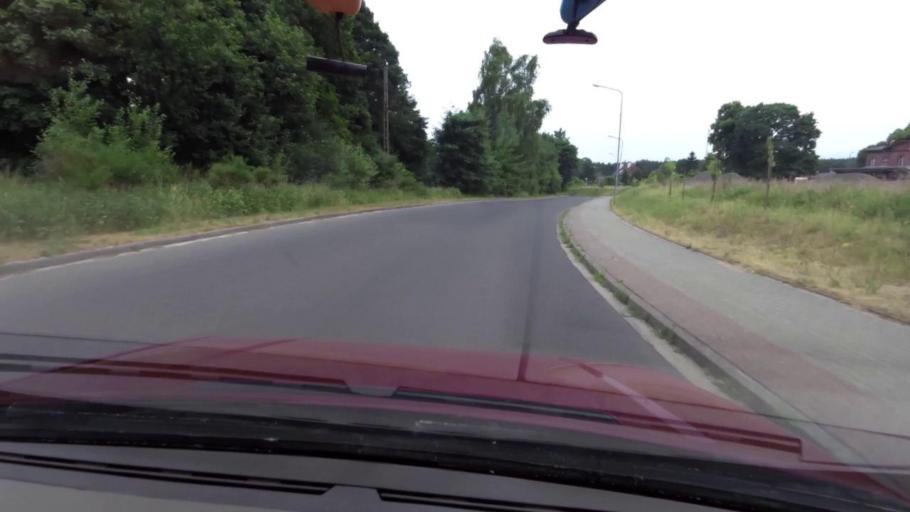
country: PL
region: Pomeranian Voivodeship
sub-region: Powiat slupski
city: Kepice
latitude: 54.2412
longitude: 16.8918
